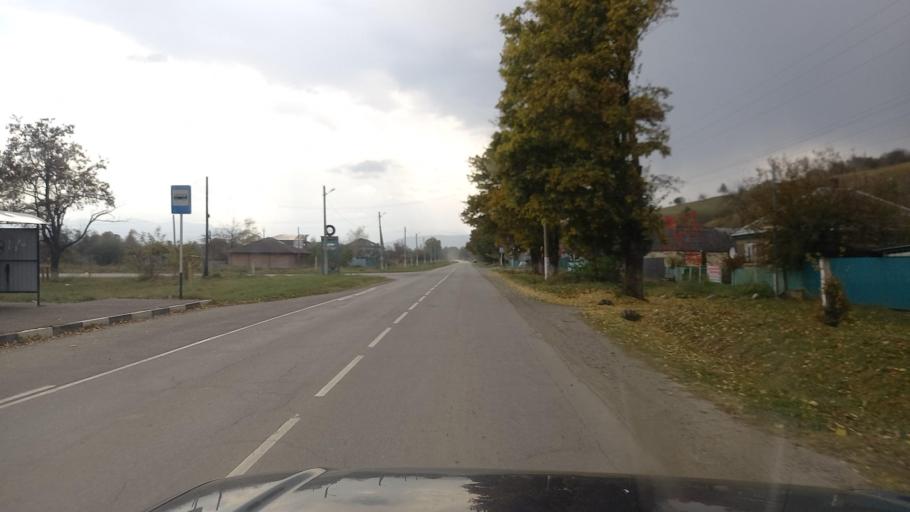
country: RU
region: Krasnodarskiy
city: Psebay
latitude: 44.1392
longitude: 40.8199
